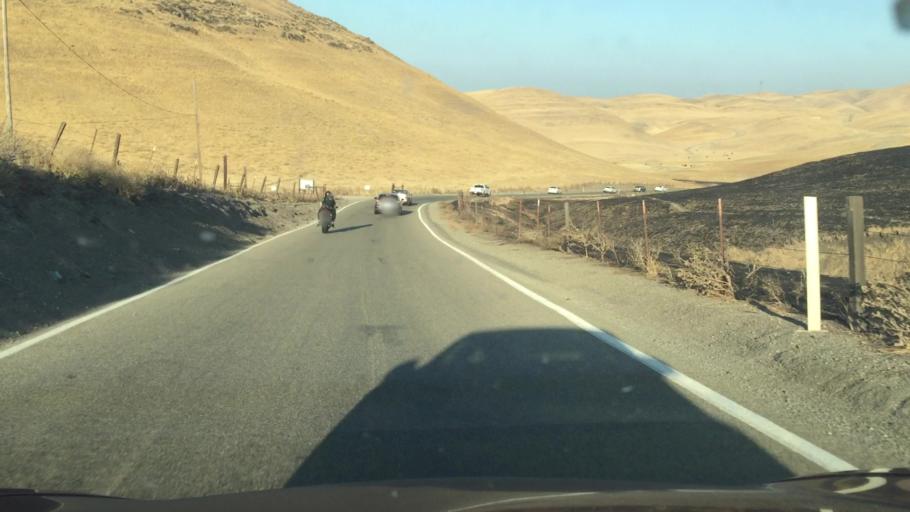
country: US
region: California
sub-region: San Joaquin County
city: Mountain House
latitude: 37.6873
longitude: -121.6062
